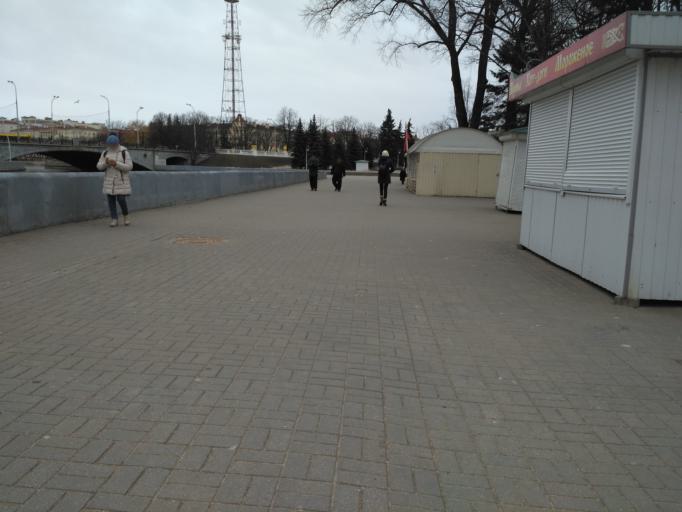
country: BY
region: Minsk
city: Minsk
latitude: 53.9053
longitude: 27.5715
